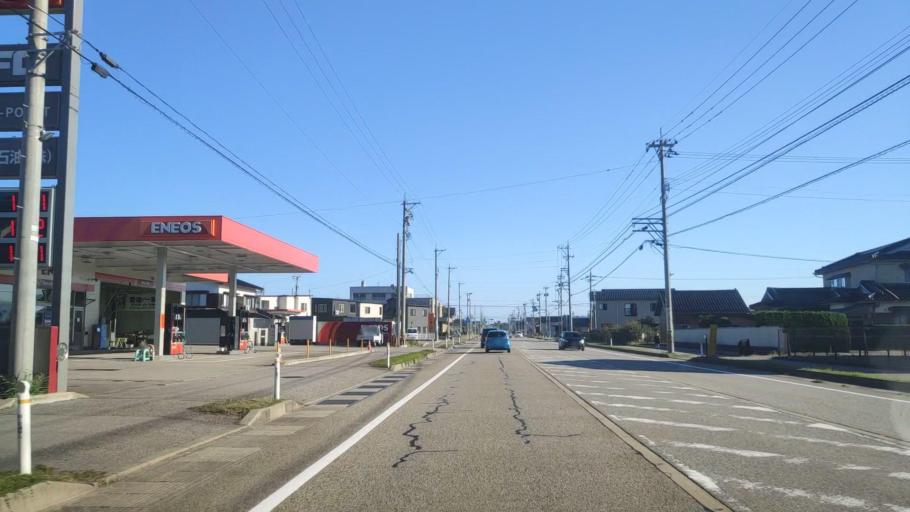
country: JP
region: Ishikawa
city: Tsubata
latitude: 36.7448
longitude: 136.7088
